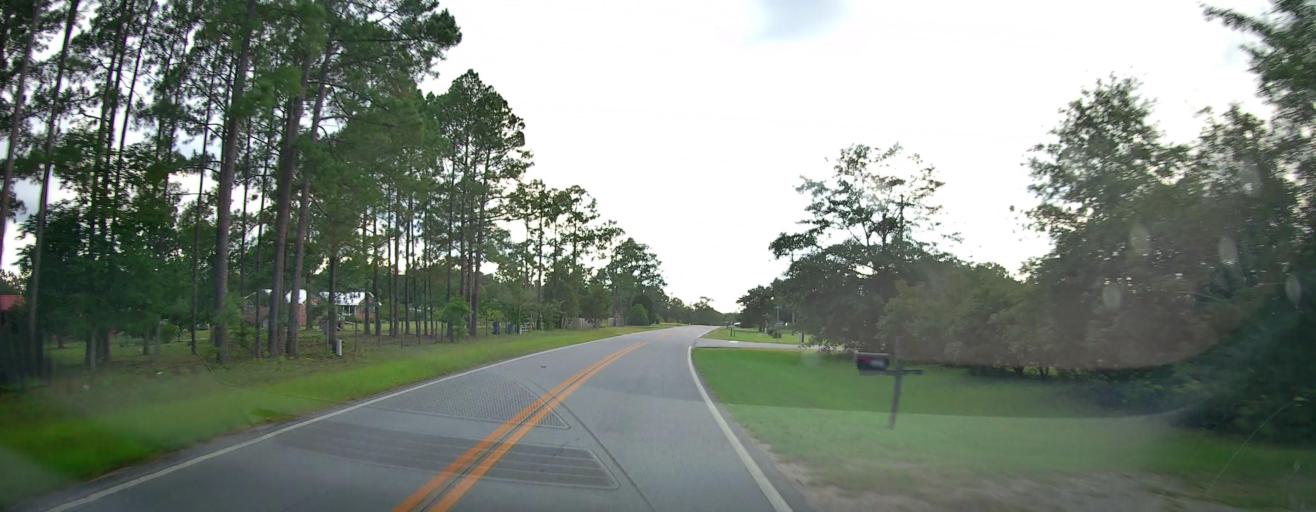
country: US
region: Georgia
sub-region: Crawford County
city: Knoxville
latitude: 32.7529
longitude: -83.9048
